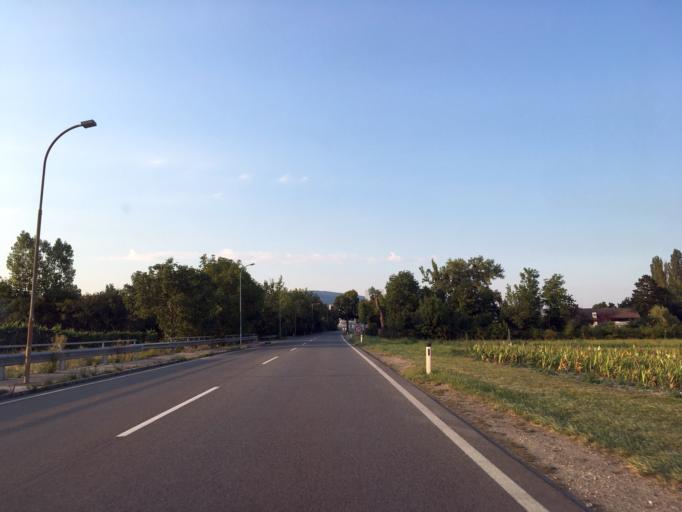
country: AT
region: Lower Austria
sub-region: Politischer Bezirk Baden
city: Baden
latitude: 47.9872
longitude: 16.2237
